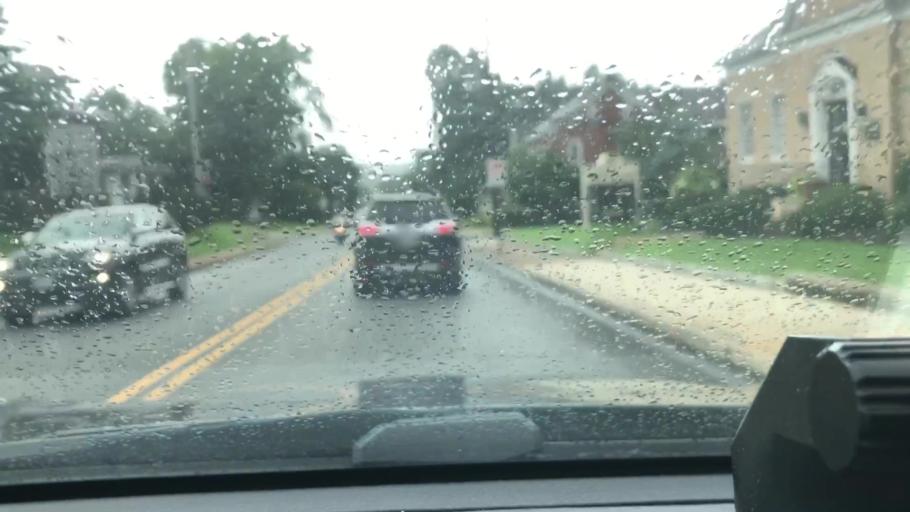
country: US
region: Pennsylvania
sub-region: Montgomery County
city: Pennsburg
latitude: 40.3988
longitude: -75.4965
